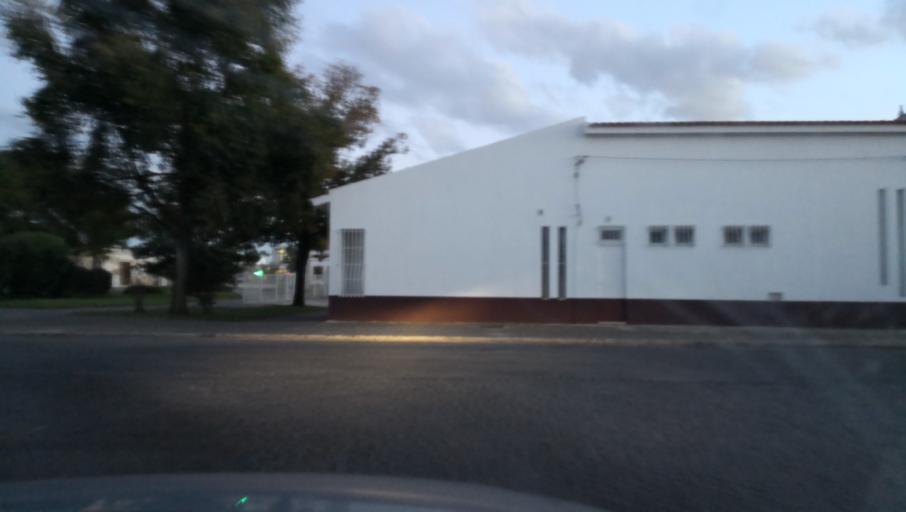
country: PT
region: Setubal
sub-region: Moita
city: Alhos Vedros
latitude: 38.6542
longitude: -9.0289
